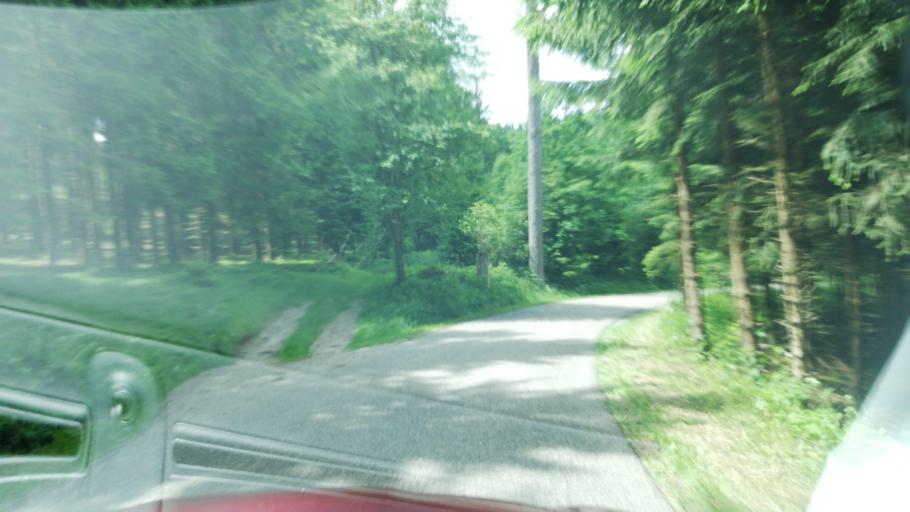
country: AT
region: Upper Austria
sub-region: Politischer Bezirk Urfahr-Umgebung
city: Haibach im Muhlkreis
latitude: 48.4357
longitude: 14.3471
